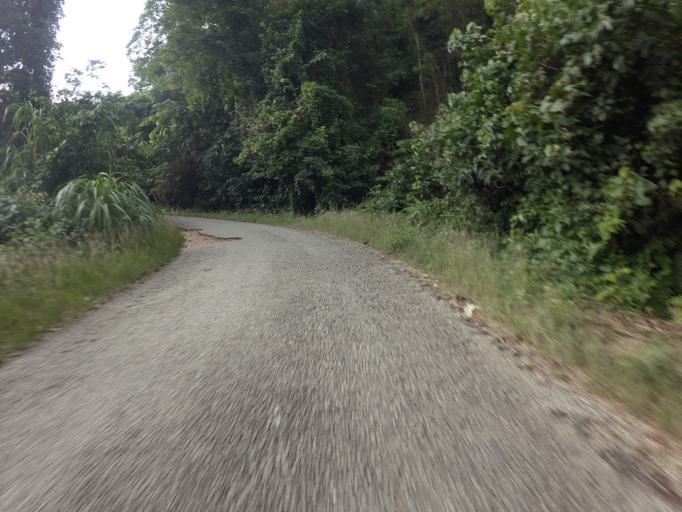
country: GH
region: Volta
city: Kpandu
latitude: 6.8287
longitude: 0.4251
